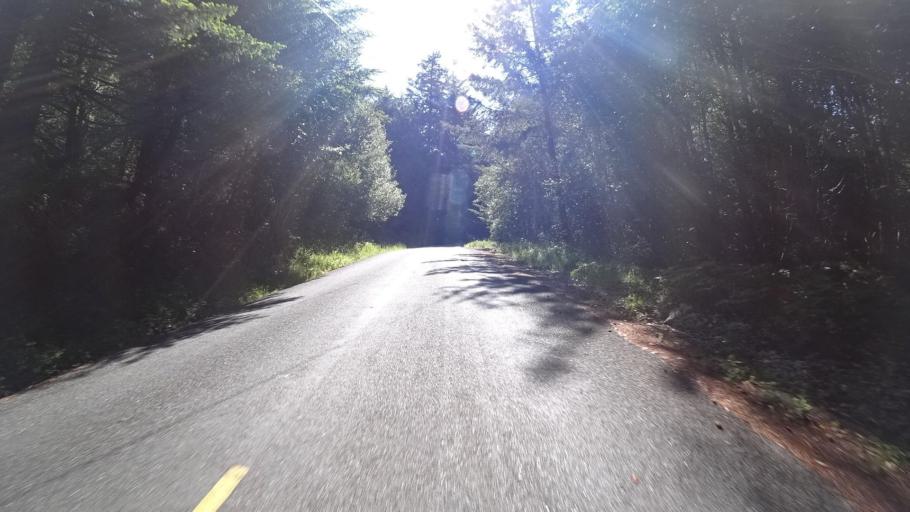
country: US
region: California
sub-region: Humboldt County
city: Rio Dell
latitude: 40.2701
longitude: -124.2125
